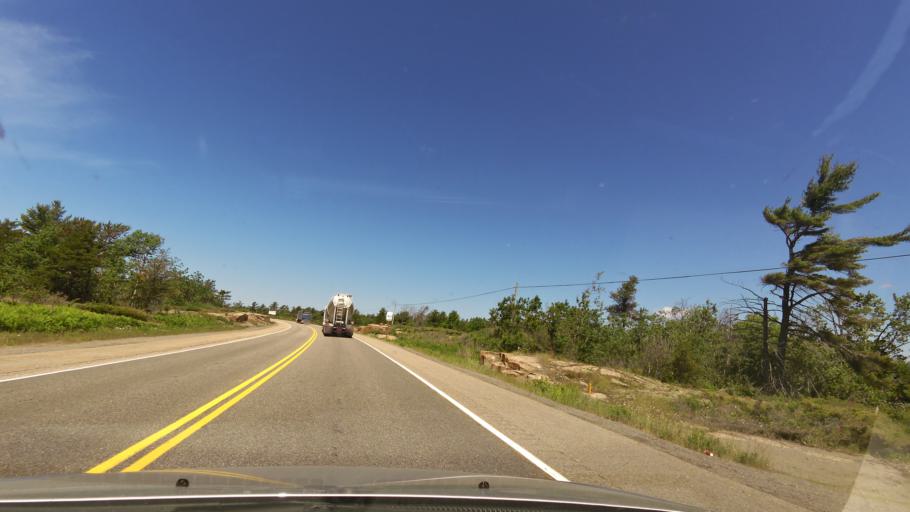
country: CA
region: Ontario
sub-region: Parry Sound District
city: Parry Sound
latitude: 45.7794
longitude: -80.5021
